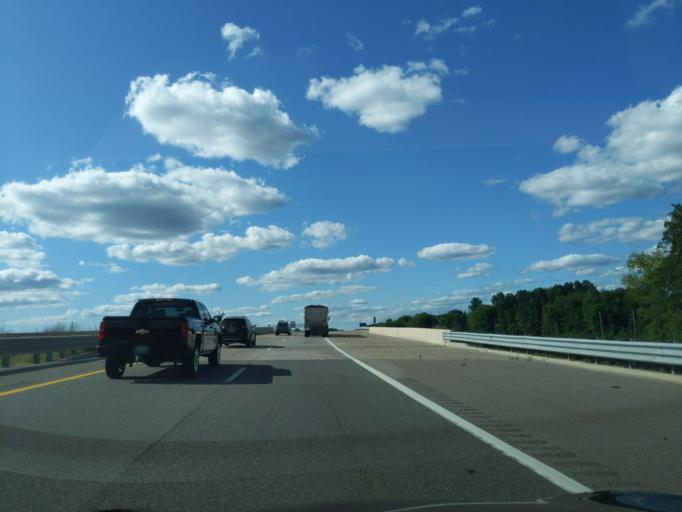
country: US
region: Michigan
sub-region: Muskegon County
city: Fruitport
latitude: 43.0768
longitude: -86.0841
